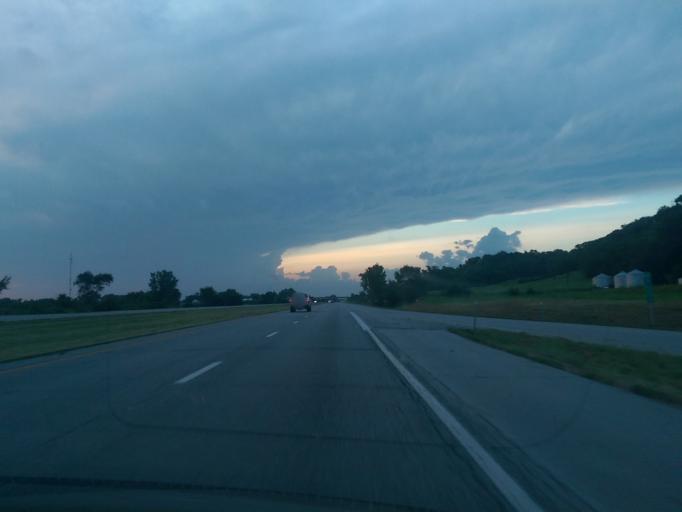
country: US
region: Iowa
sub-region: Fremont County
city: Hamburg
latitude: 40.5520
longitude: -95.6290
